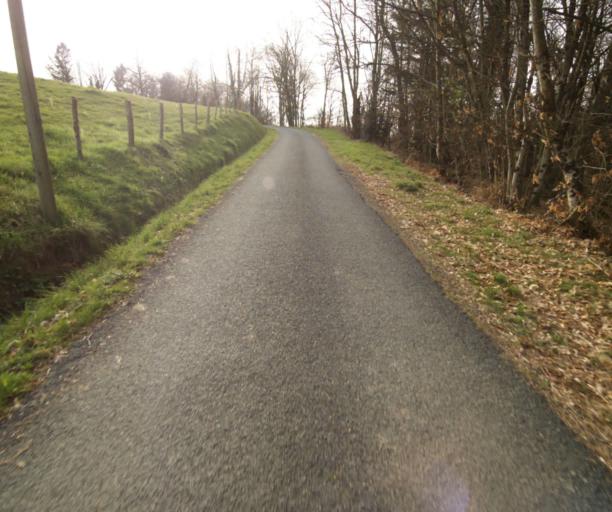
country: FR
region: Limousin
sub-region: Departement de la Correze
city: Chamboulive
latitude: 45.4518
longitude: 1.7501
